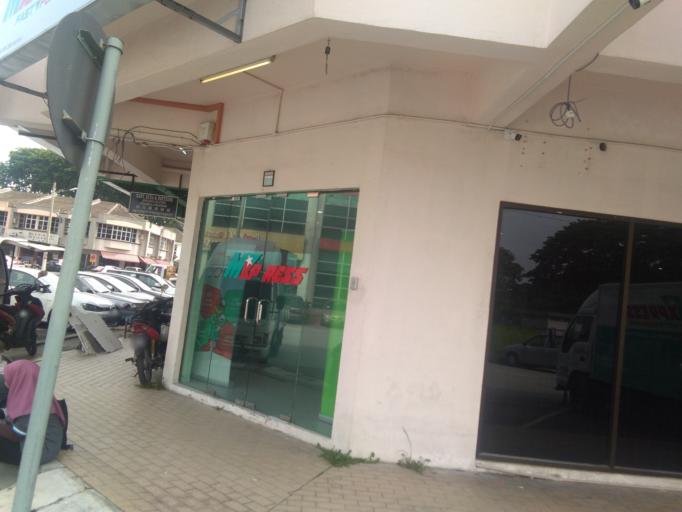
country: MY
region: Perak
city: Ipoh
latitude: 4.6067
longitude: 101.0817
